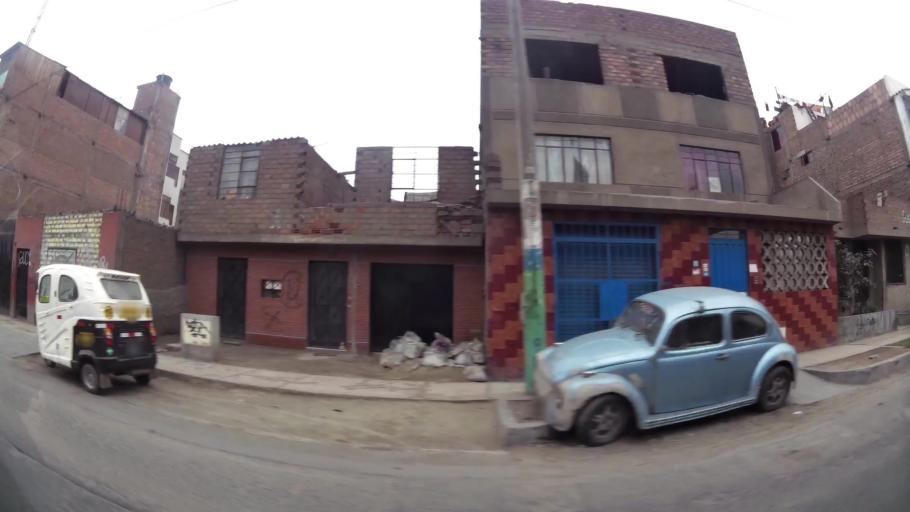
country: PE
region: Lima
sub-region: Lima
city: San Luis
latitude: -12.0468
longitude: -76.9787
